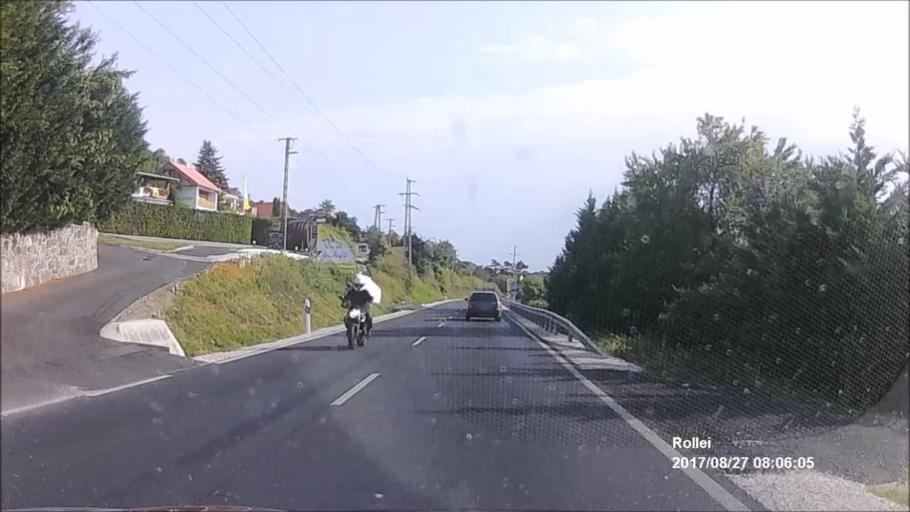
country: HU
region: Zala
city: Vonyarcvashegy
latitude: 46.7670
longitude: 17.3571
